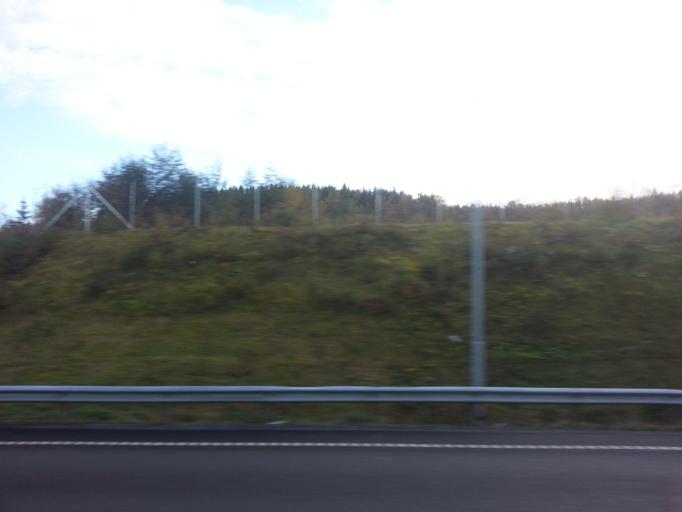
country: NO
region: Sor-Trondelag
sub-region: Malvik
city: Malvik
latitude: 63.4253
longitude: 10.7217
